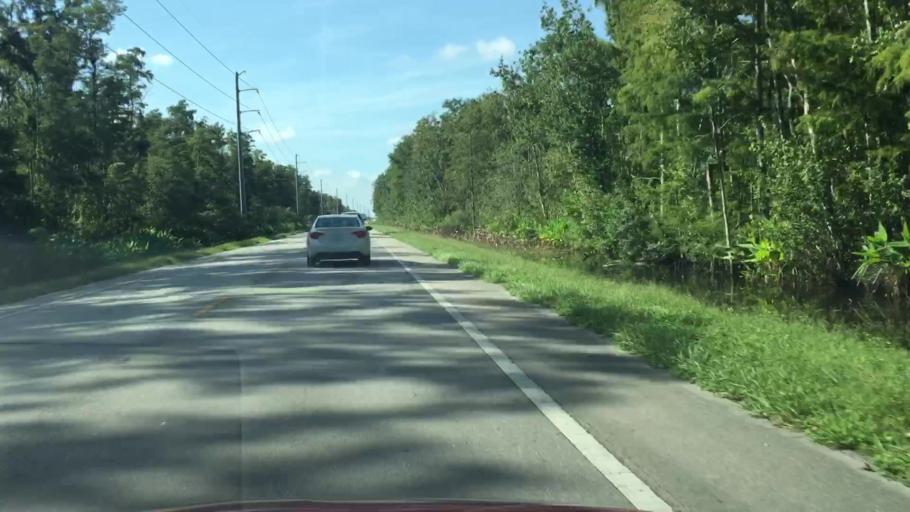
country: US
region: Florida
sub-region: Collier County
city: Orangetree
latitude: 26.3409
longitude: -81.5952
